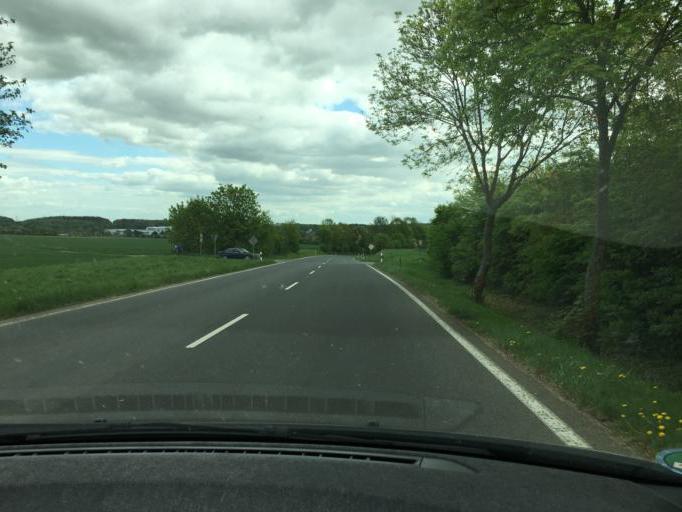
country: DE
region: North Rhine-Westphalia
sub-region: Regierungsbezirk Koln
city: Mechernich
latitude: 50.6359
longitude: 6.6811
